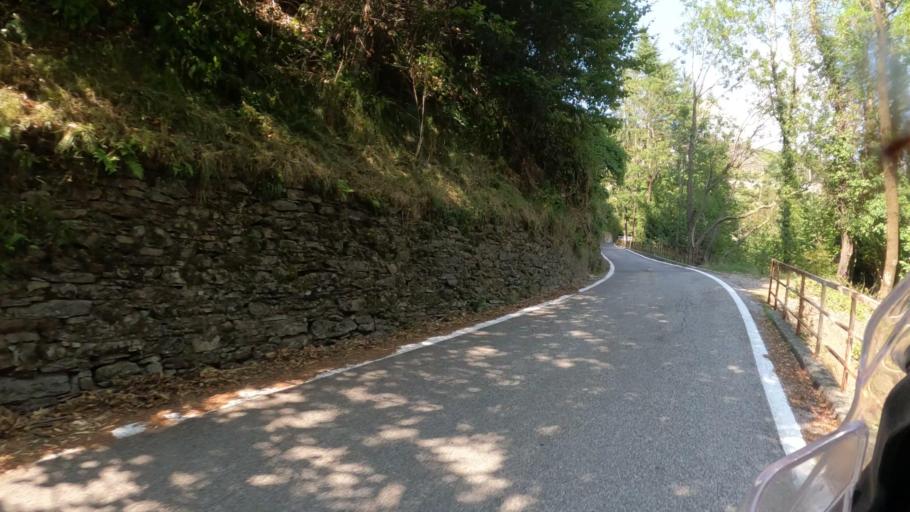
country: IT
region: Lombardy
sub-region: Provincia di Varese
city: Veddasca
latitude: 46.0639
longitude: 8.7815
